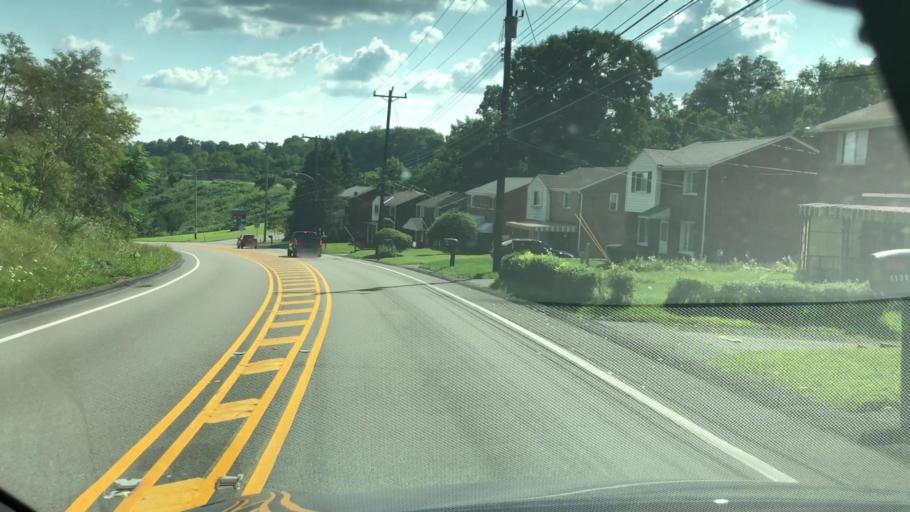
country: US
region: Pennsylvania
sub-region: Allegheny County
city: East McKeesport
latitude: 40.3660
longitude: -79.7838
